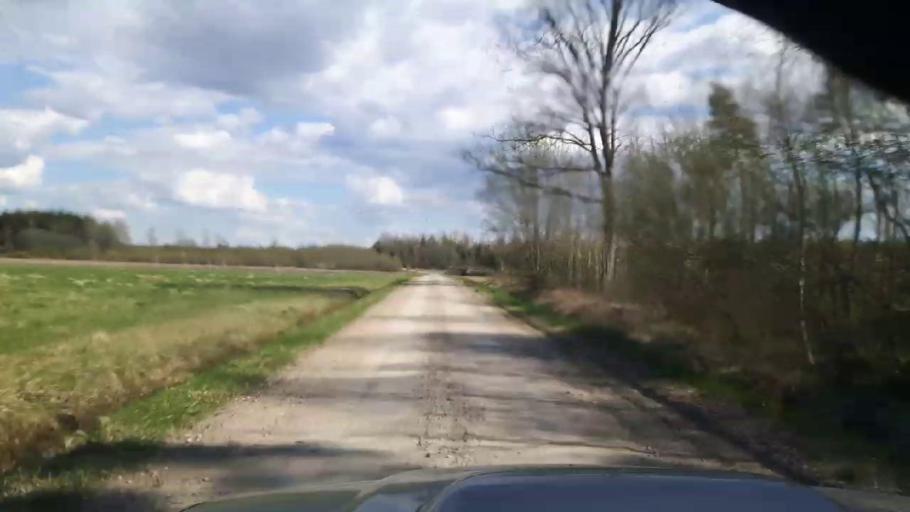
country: EE
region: Paernumaa
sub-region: Tootsi vald
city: Tootsi
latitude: 58.4477
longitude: 24.8380
